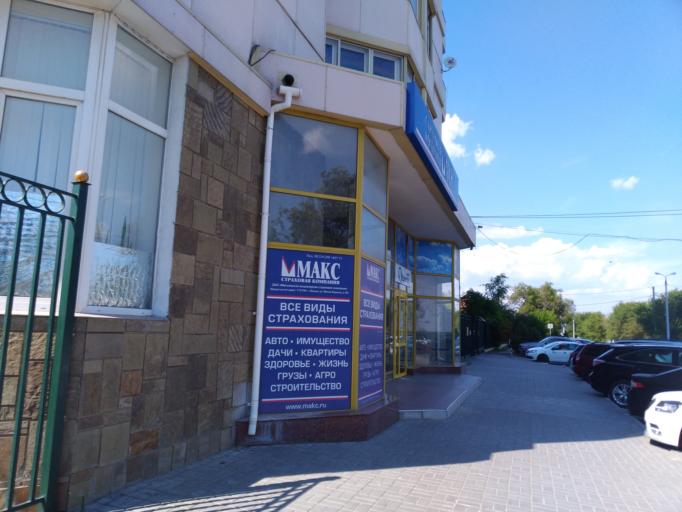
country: RU
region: Volgograd
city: Volgograd
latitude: 48.7189
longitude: 44.5372
